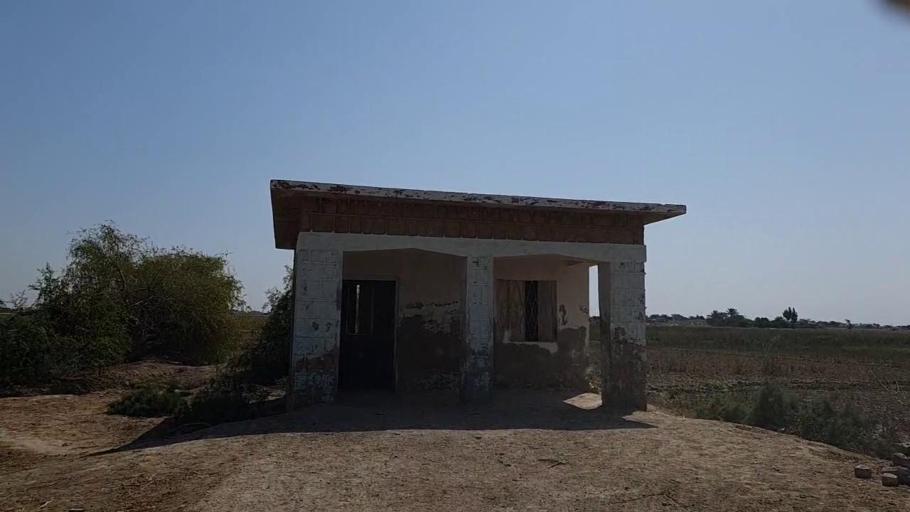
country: PK
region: Sindh
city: Mirpur Batoro
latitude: 24.6712
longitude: 68.3059
